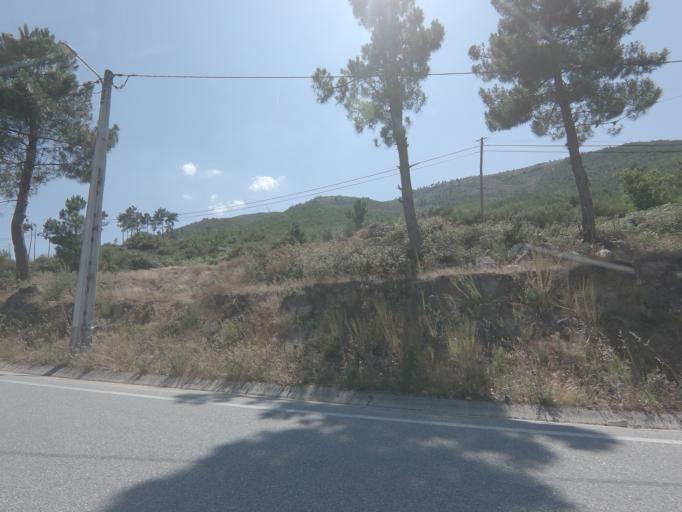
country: PT
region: Viseu
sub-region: Tarouca
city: Tarouca
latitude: 41.0059
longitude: -7.7819
